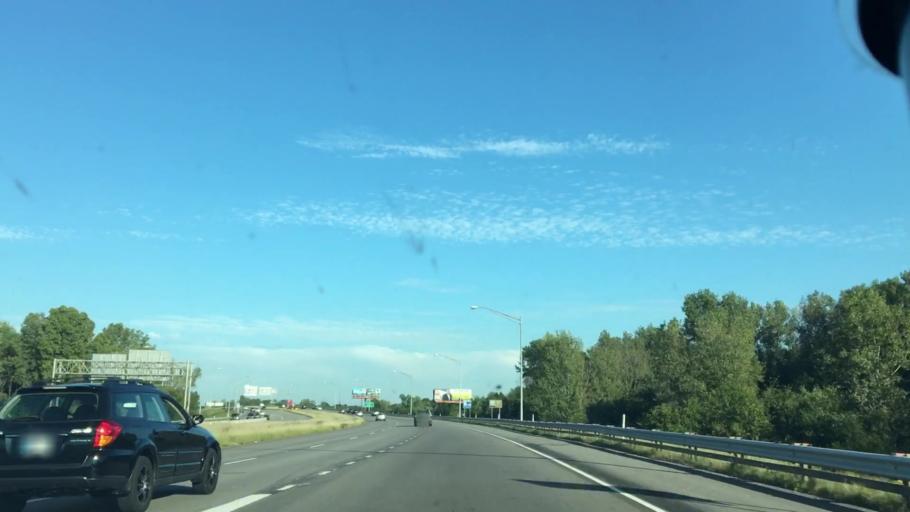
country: US
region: Indiana
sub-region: Vanderburgh County
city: Evansville
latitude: 37.9368
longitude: -87.5364
